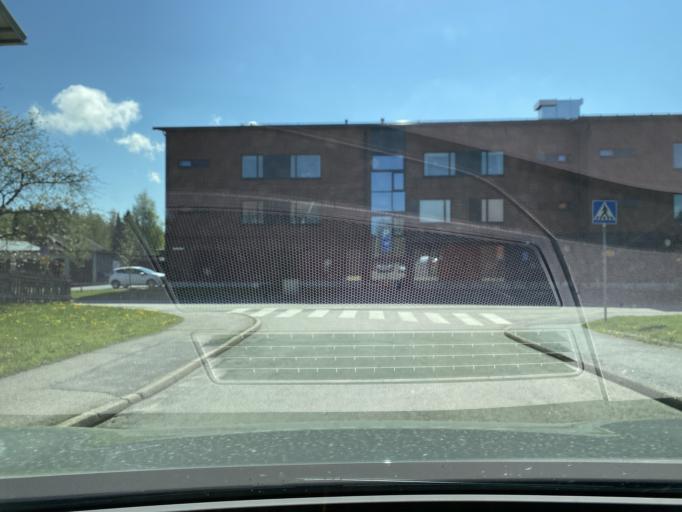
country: FI
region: Pirkanmaa
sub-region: Lounais-Pirkanmaa
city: Vammala
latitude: 61.3376
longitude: 22.9089
